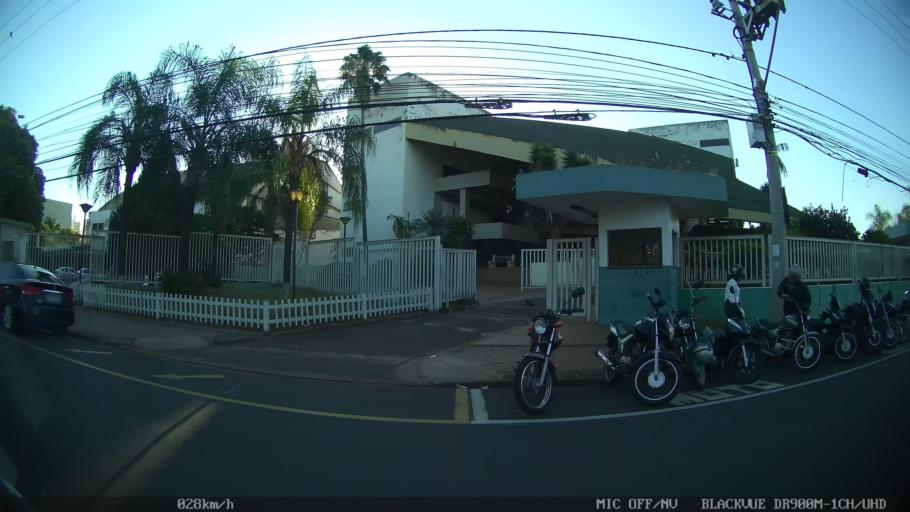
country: BR
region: Sao Paulo
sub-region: Sao Jose Do Rio Preto
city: Sao Jose do Rio Preto
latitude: -20.8069
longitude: -49.3774
